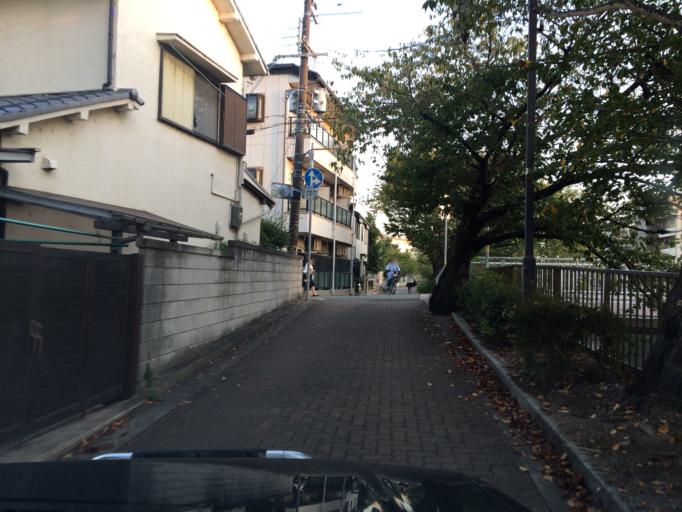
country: JP
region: Hyogo
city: Amagasaki
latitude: 34.7466
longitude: 135.4102
